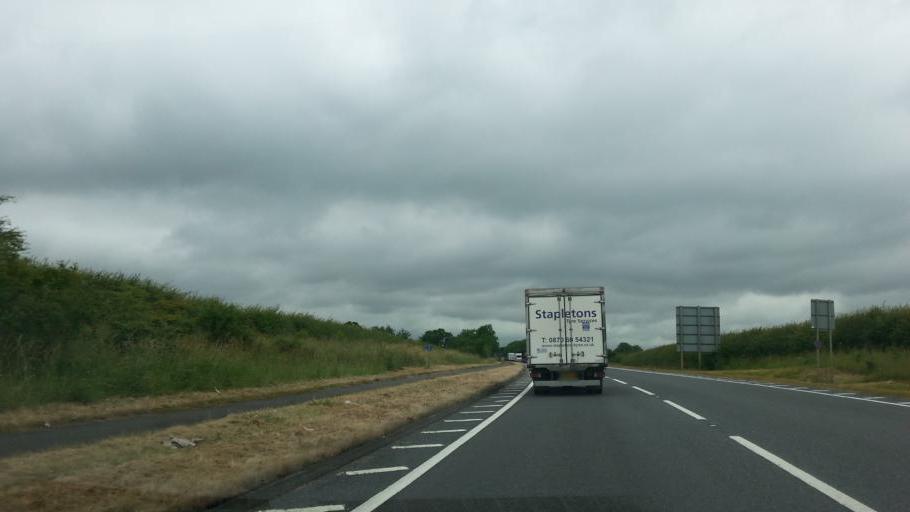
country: GB
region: England
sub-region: Northamptonshire
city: Broughton
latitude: 52.3687
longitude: -0.7845
